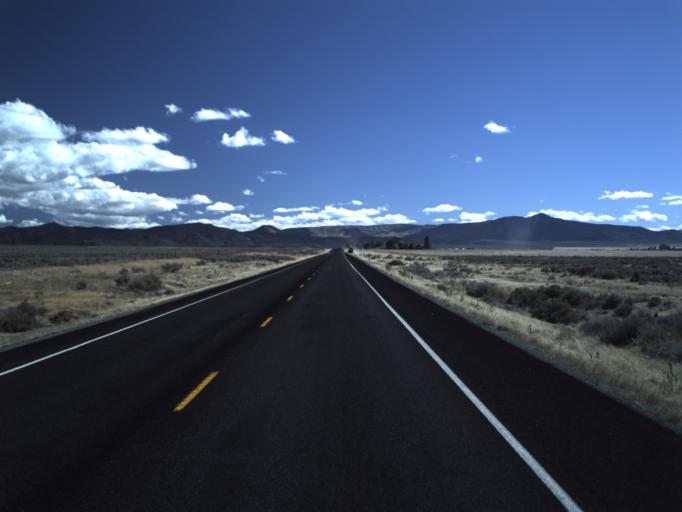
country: US
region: Utah
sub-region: Beaver County
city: Milford
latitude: 38.2759
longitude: -112.9606
